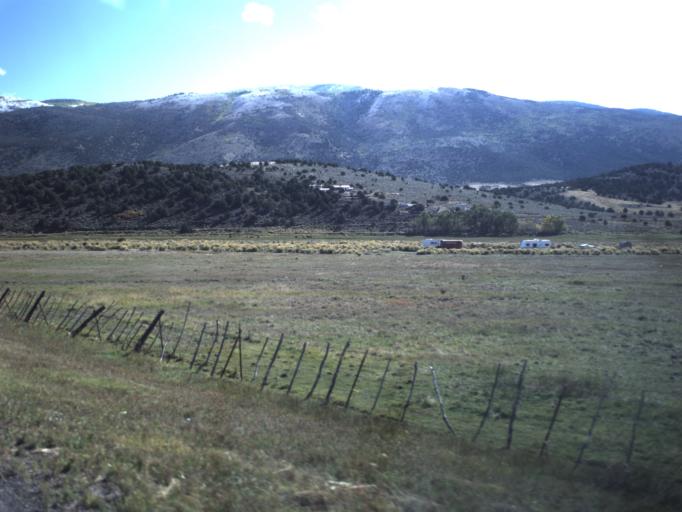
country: US
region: Utah
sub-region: Wayne County
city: Loa
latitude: 38.5594
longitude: -111.8580
